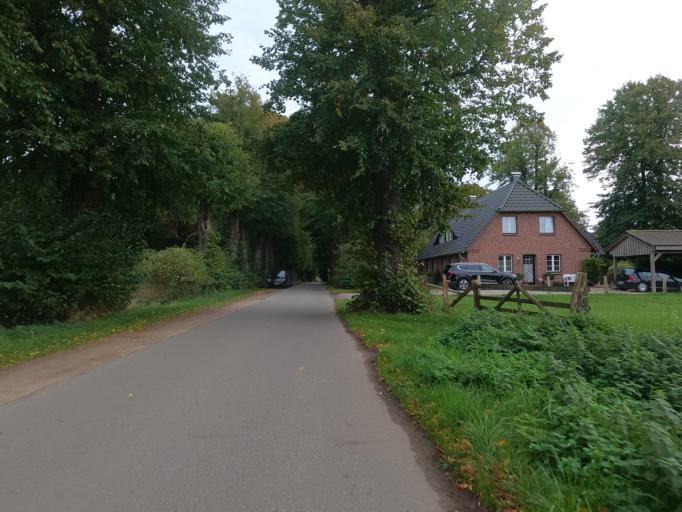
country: DE
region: Schleswig-Holstein
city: Neukirchen
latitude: 54.2917
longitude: 11.0563
